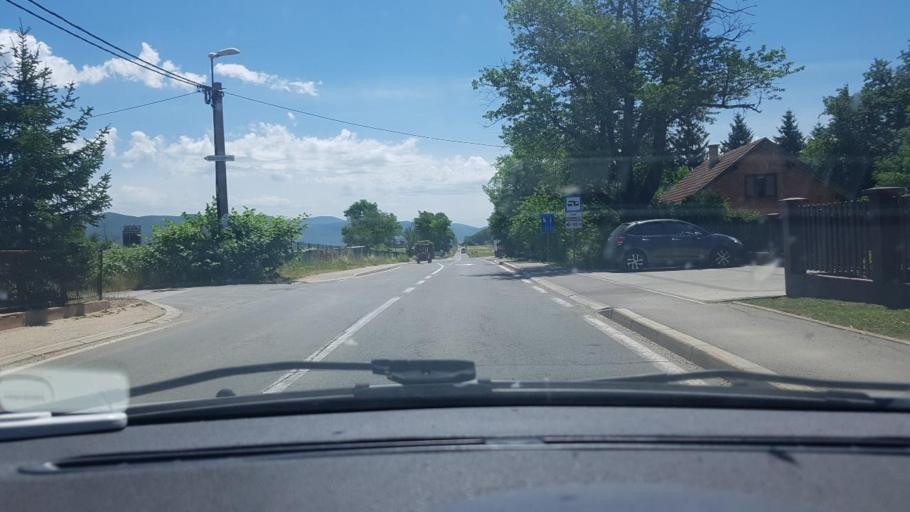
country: HR
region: Licko-Senjska
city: Otocac
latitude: 44.8617
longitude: 15.2632
